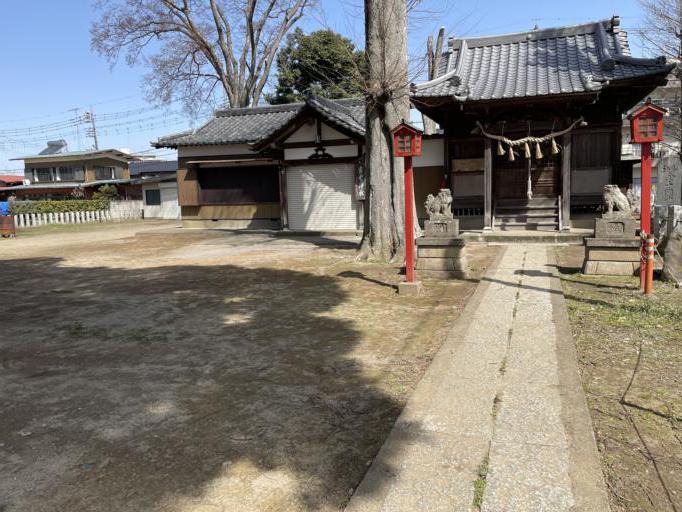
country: JP
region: Ibaraki
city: Koga
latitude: 36.1985
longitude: 139.7152
